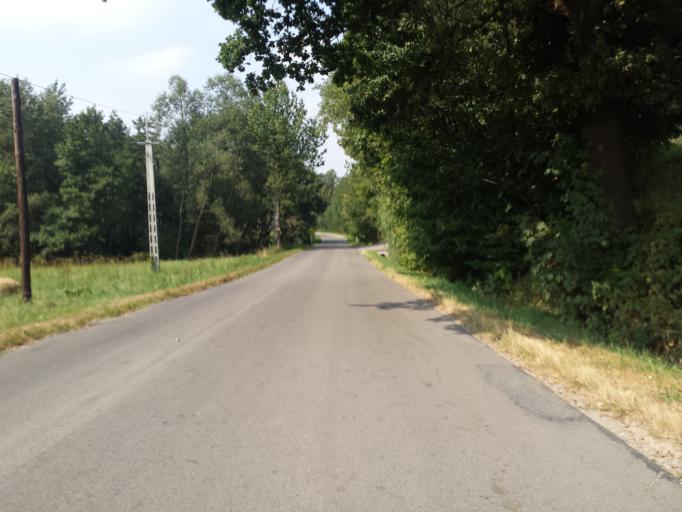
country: PL
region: Subcarpathian Voivodeship
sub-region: Powiat rzeszowski
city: Blazowa
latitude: 49.8504
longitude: 22.1399
